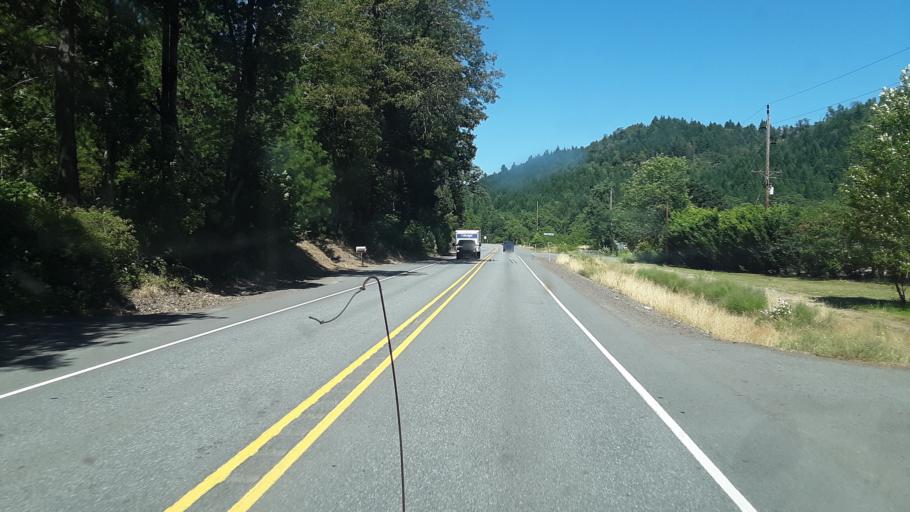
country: US
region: Oregon
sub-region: Josephine County
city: Redwood
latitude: 42.3636
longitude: -123.5138
